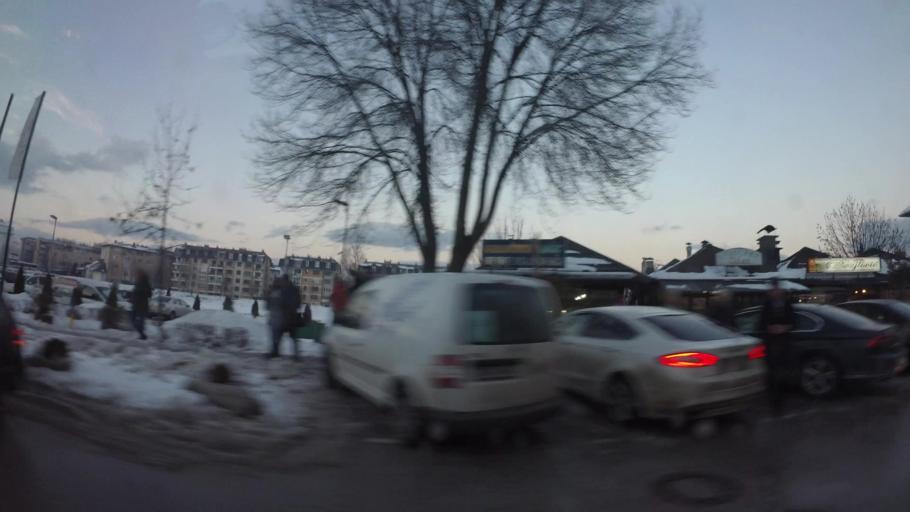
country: BA
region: Federation of Bosnia and Herzegovina
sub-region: Kanton Sarajevo
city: Sarajevo
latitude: 43.8300
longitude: 18.3033
